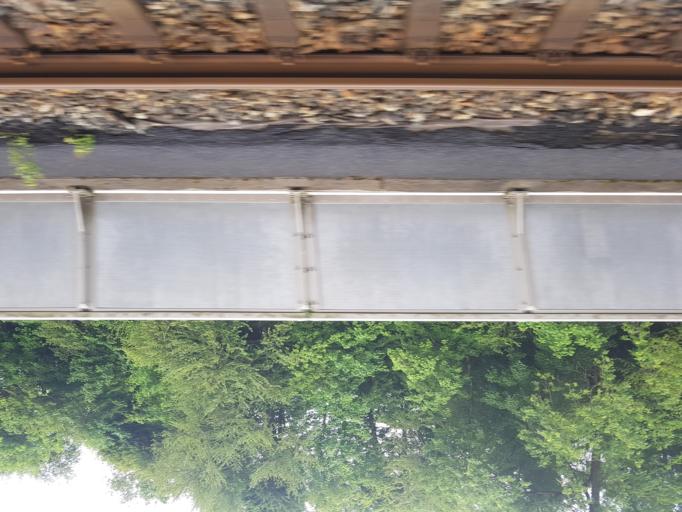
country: NO
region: Hordaland
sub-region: Bergen
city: Sandsli
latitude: 60.3269
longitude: 5.3465
